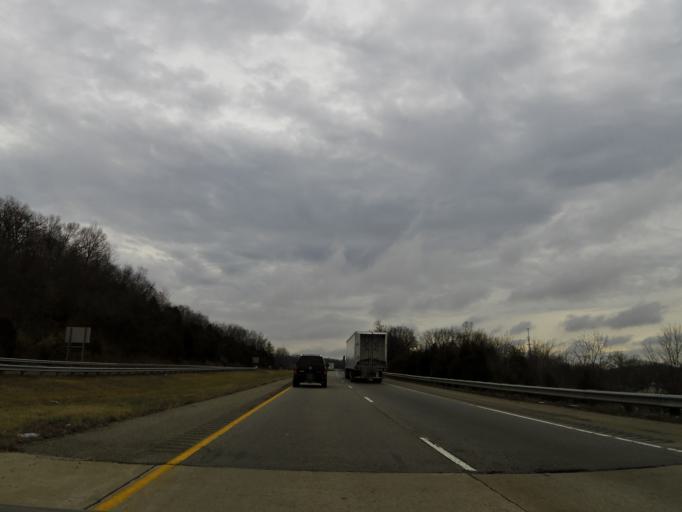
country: US
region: Ohio
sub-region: Hamilton County
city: Harrison
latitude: 39.2780
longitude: -84.8243
